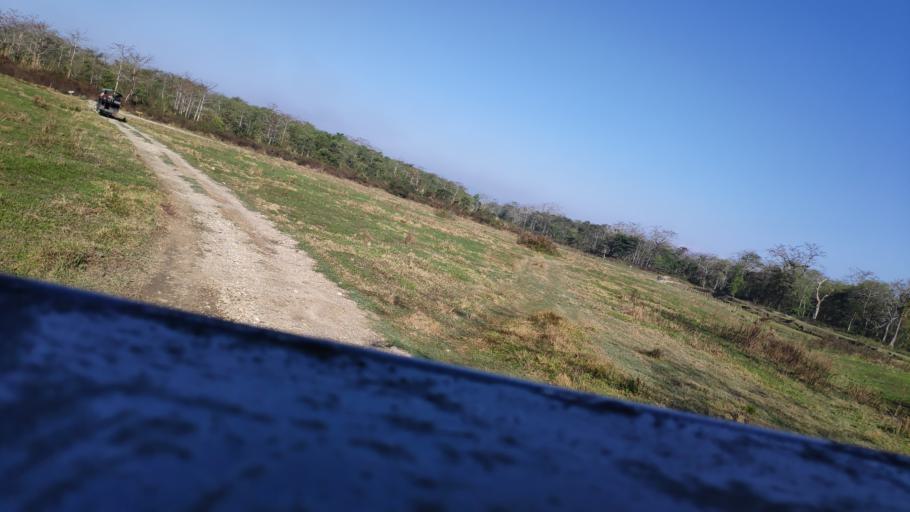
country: NP
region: Central Region
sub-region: Narayani Zone
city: Bharatpur
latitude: 27.5604
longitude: 84.5234
